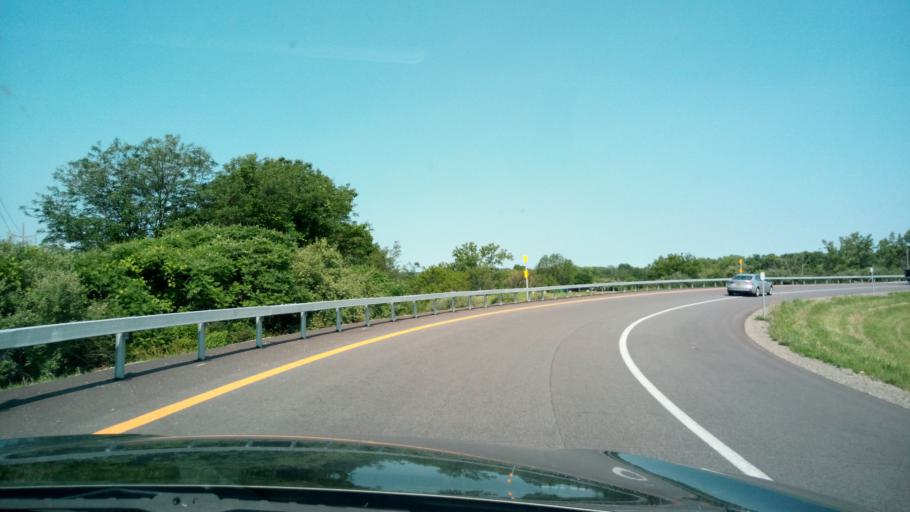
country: US
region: New York
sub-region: Chemung County
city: Horseheads
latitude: 42.1600
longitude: -76.8477
